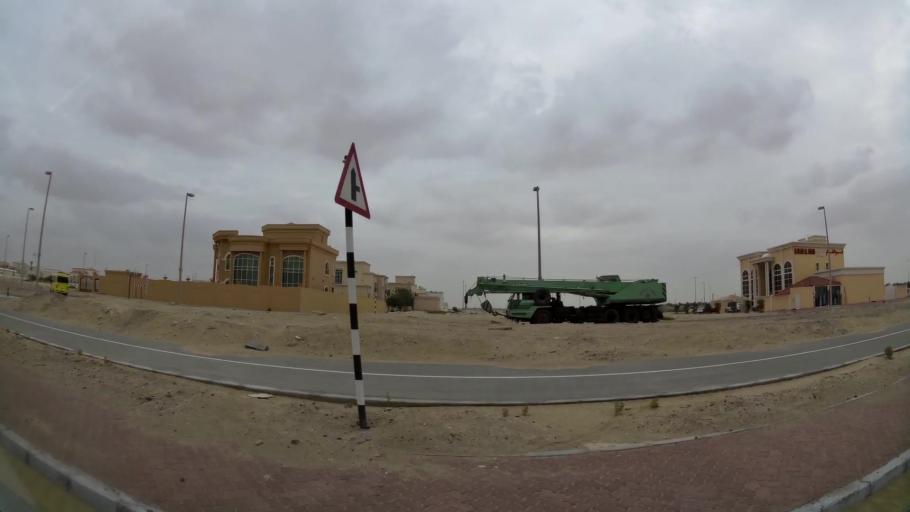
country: AE
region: Abu Dhabi
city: Abu Dhabi
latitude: 24.3716
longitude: 54.6499
